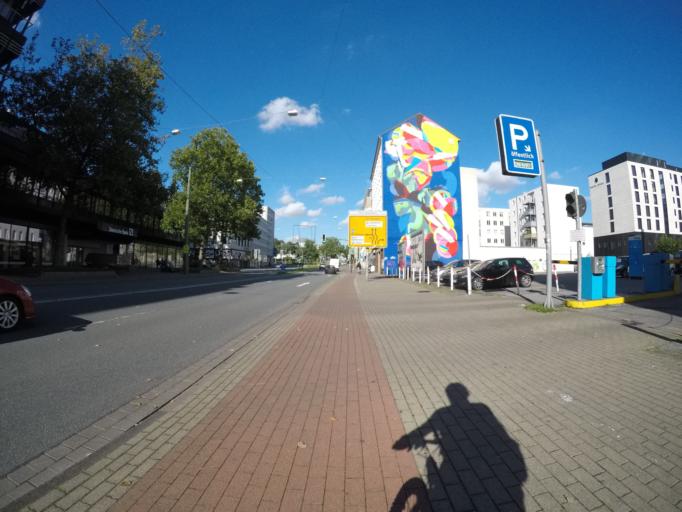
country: DE
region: North Rhine-Westphalia
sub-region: Regierungsbezirk Detmold
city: Bielefeld
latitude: 52.0254
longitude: 8.5349
